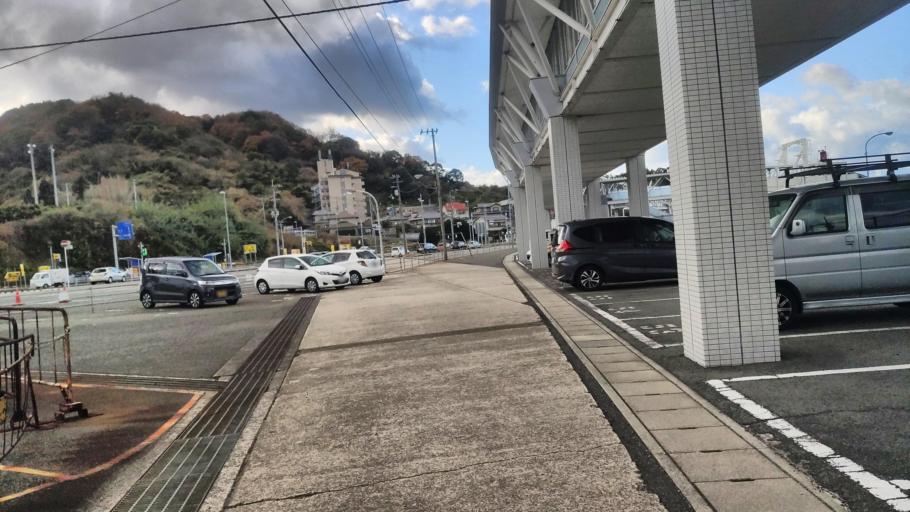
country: JP
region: Ehime
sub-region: Shikoku-chuo Shi
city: Matsuyama
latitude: 33.8903
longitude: 132.7058
